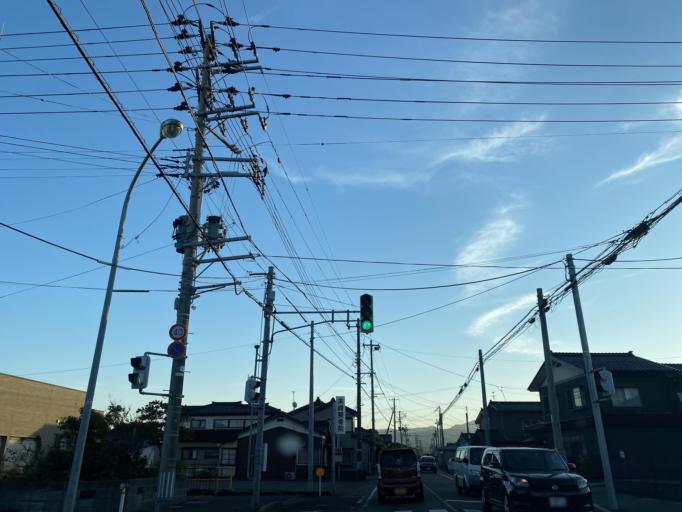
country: JP
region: Niigata
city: Kashiwazaki
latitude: 37.3802
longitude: 138.5673
